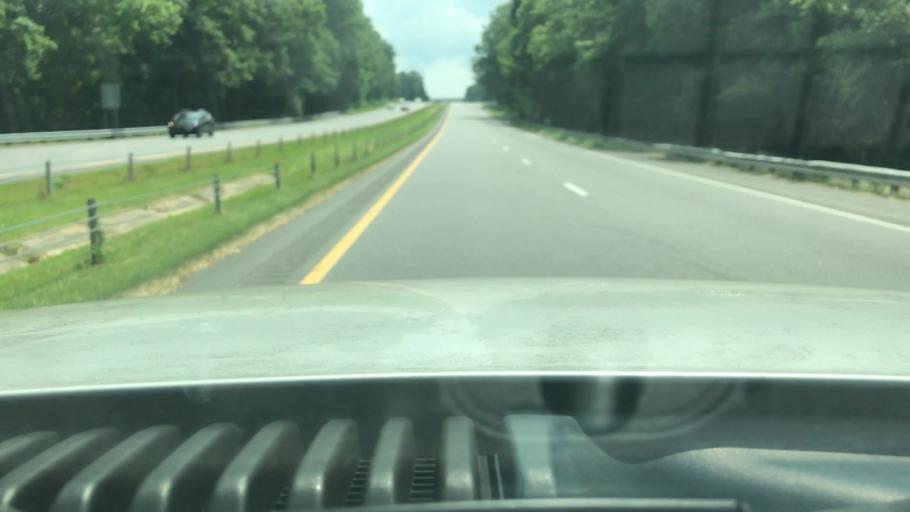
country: US
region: North Carolina
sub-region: Wilkes County
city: Wilkesboro
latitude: 36.1356
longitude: -81.1545
